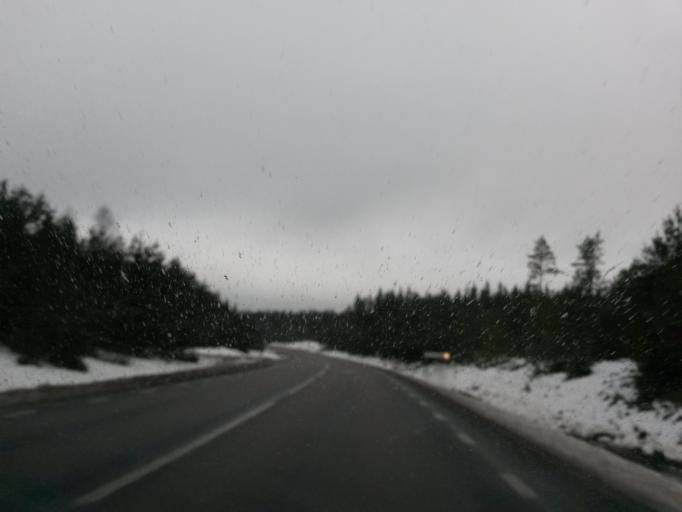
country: SE
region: Vaestra Goetaland
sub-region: Boras Kommun
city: Sandared
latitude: 57.7934
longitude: 12.7684
